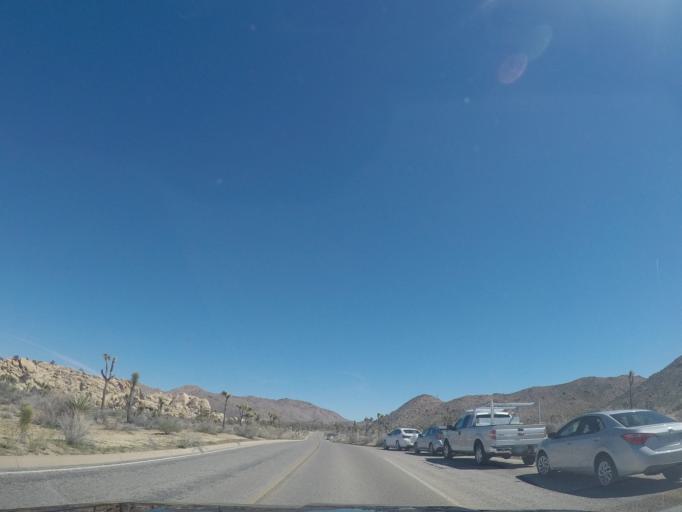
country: US
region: California
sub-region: San Bernardino County
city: Twentynine Palms
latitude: 34.0217
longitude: -116.1471
